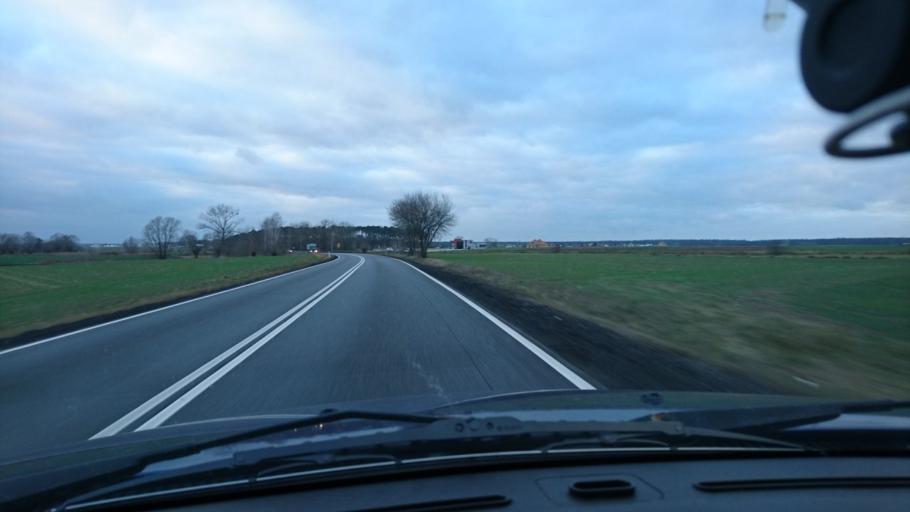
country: PL
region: Greater Poland Voivodeship
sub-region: Powiat kepinski
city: Opatow
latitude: 51.2201
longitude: 18.1356
